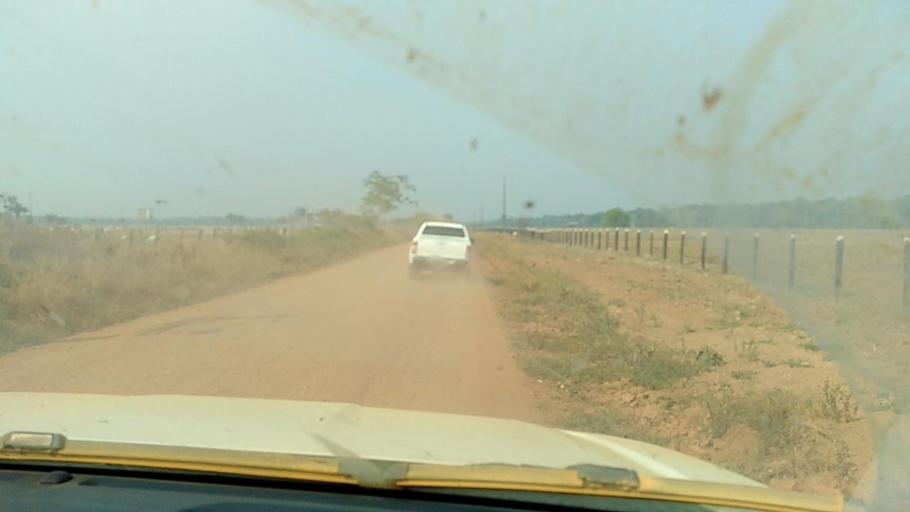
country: BR
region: Rondonia
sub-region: Porto Velho
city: Porto Velho
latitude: -8.7726
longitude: -64.0792
